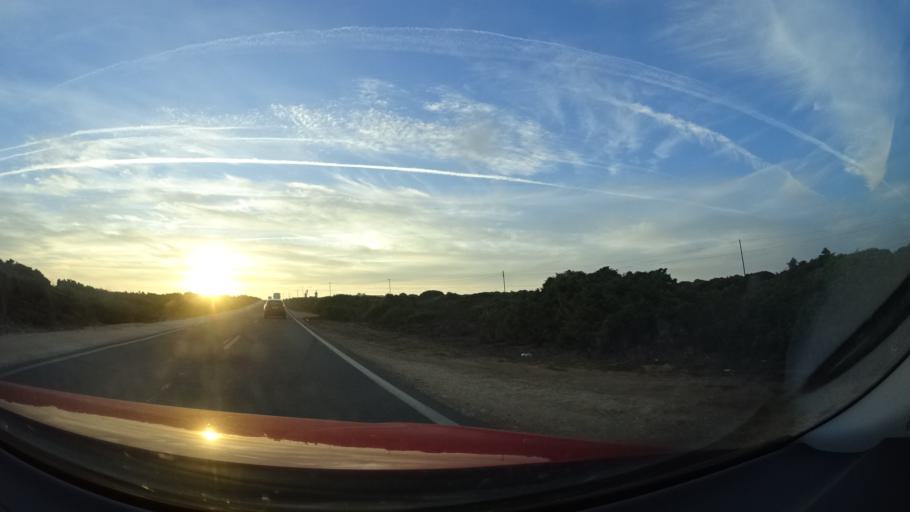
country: PT
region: Faro
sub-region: Vila do Bispo
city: Sagres
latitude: 37.0273
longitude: -8.9764
